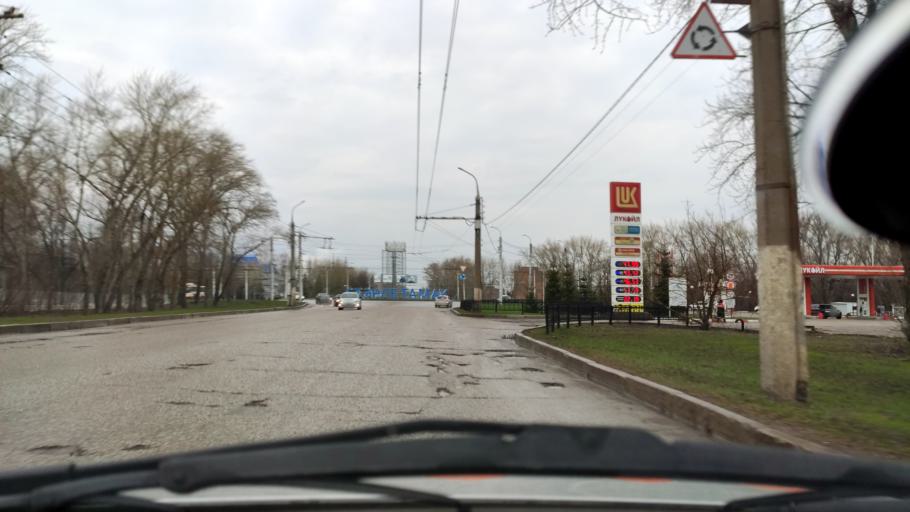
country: RU
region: Bashkortostan
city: Sterlitamak
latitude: 53.6618
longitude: 55.9490
